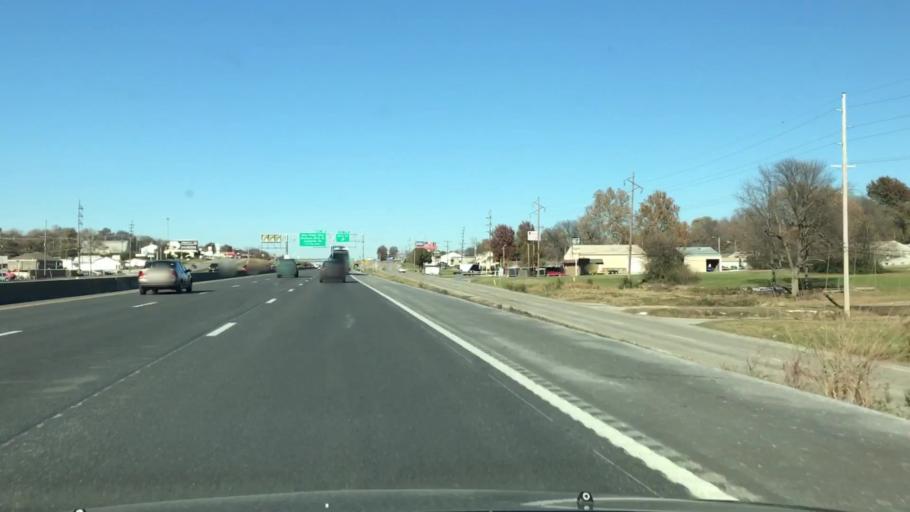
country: US
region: Missouri
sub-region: Jackson County
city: Grandview
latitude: 38.8806
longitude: -94.5256
